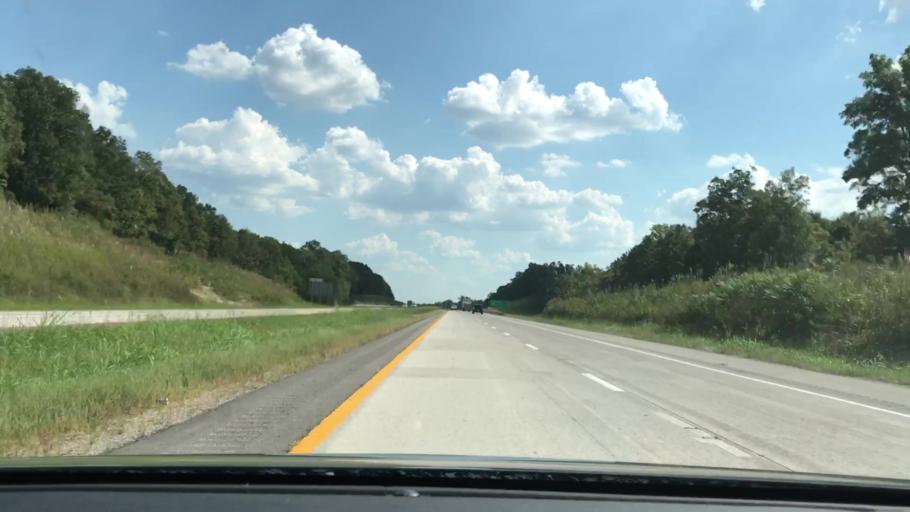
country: US
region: Kentucky
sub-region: Ohio County
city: Oak Grove
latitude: 37.3762
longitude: -86.8043
